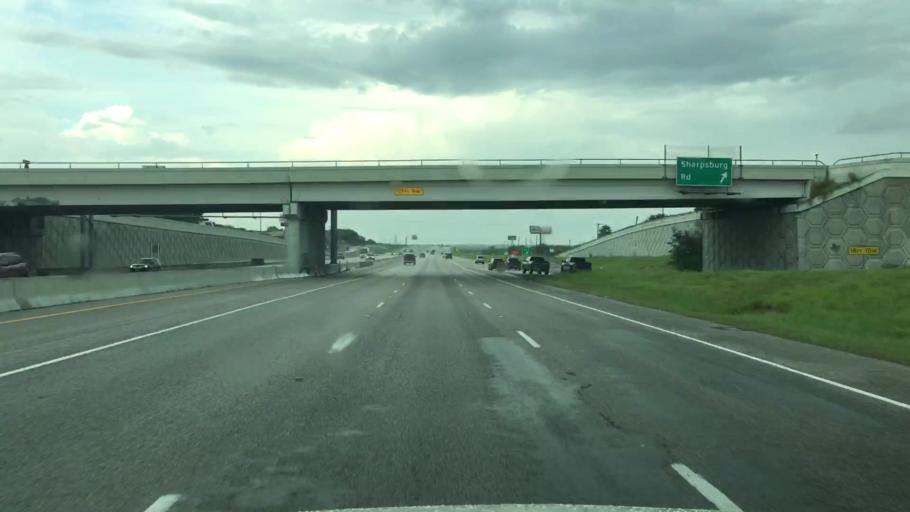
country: US
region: Texas
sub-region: Nueces County
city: Robstown
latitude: 27.8666
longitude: -97.6232
